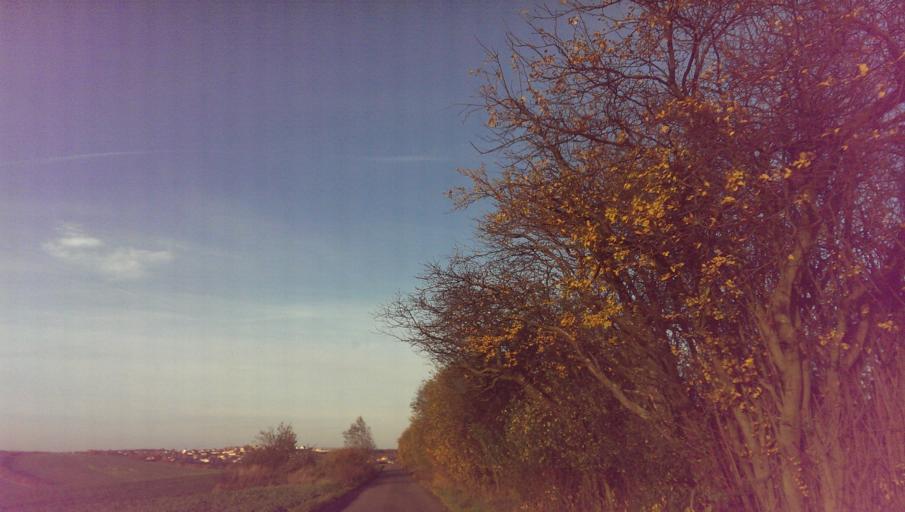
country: CZ
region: Zlin
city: Brezolupy
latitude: 49.1541
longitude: 17.5999
